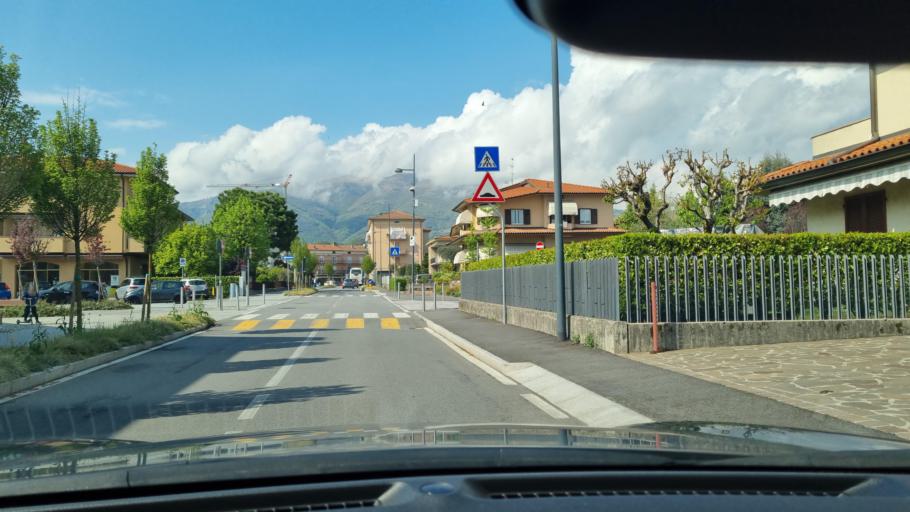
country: IT
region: Lombardy
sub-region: Provincia di Bergamo
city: Ambivere
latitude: 45.7185
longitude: 9.5497
